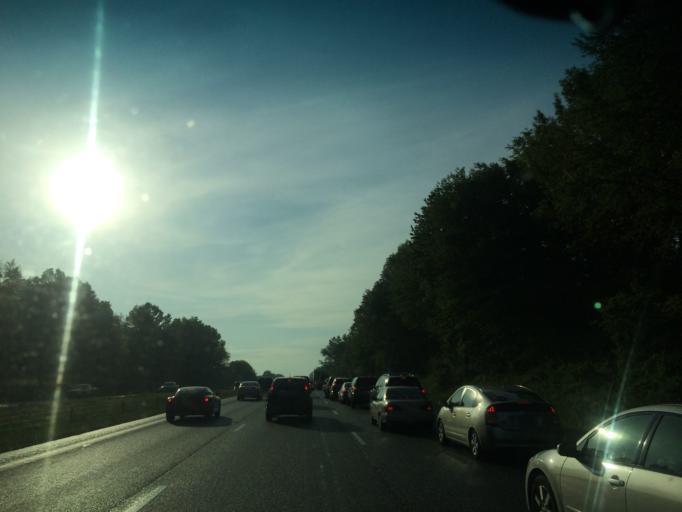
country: US
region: Maryland
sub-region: Carroll County
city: Sykesville
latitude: 39.3078
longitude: -76.9438
